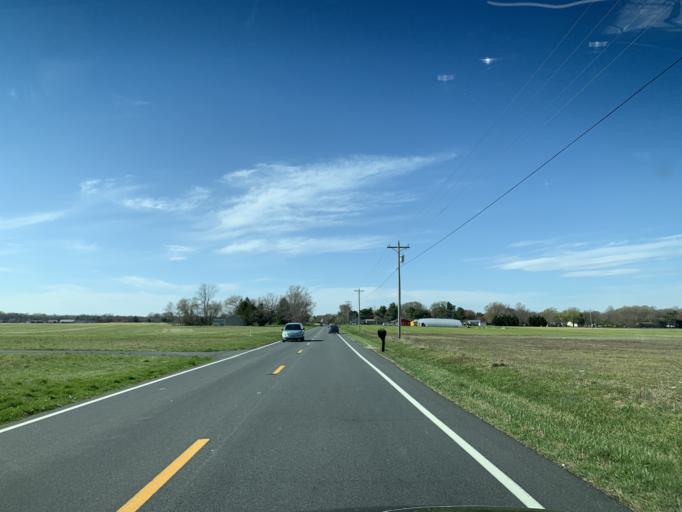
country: US
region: Delaware
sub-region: Kent County
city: Riverview
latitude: 39.0263
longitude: -75.5423
